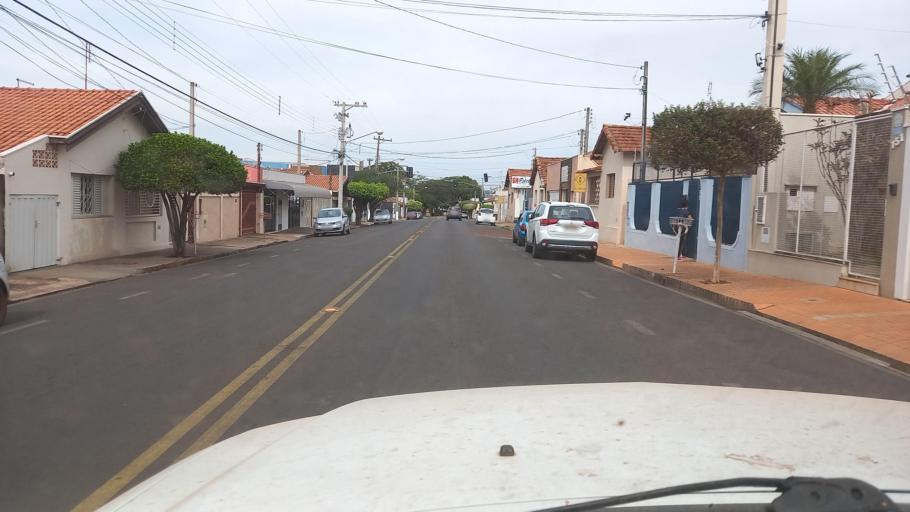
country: BR
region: Sao Paulo
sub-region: Moji-Guacu
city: Mogi-Gaucu
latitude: -22.3613
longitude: -46.9426
